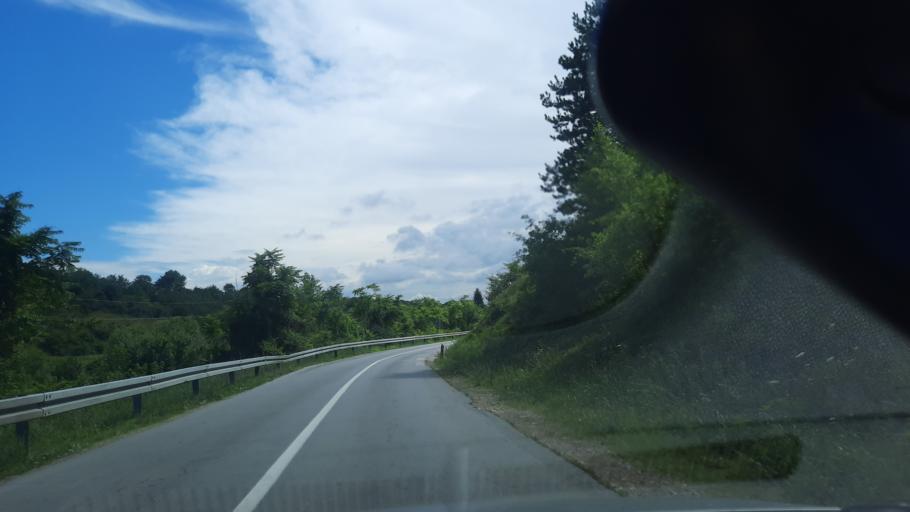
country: RS
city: Celarevo
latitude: 45.1291
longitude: 19.5740
